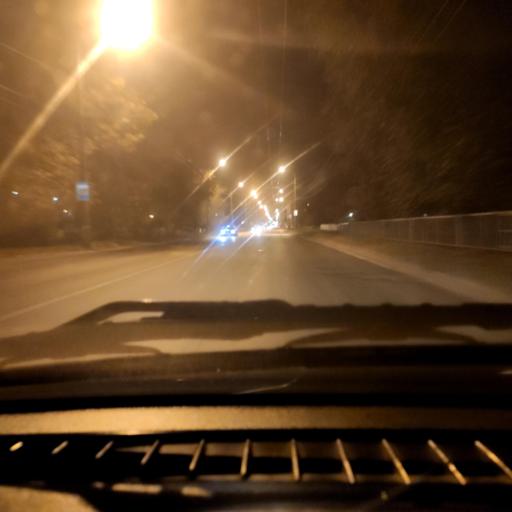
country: RU
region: Samara
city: Tol'yatti
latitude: 53.5435
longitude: 49.4448
